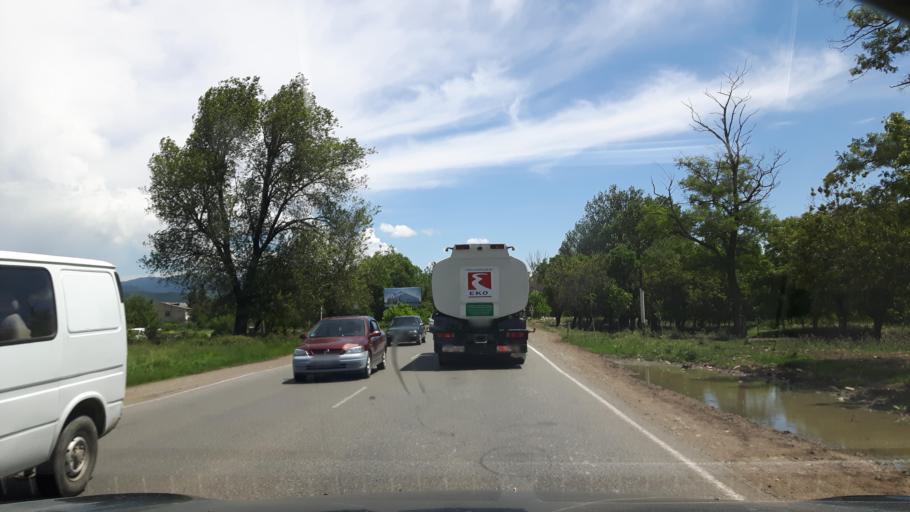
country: GE
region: Kakheti
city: Sagarejo
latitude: 41.7126
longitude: 45.1564
